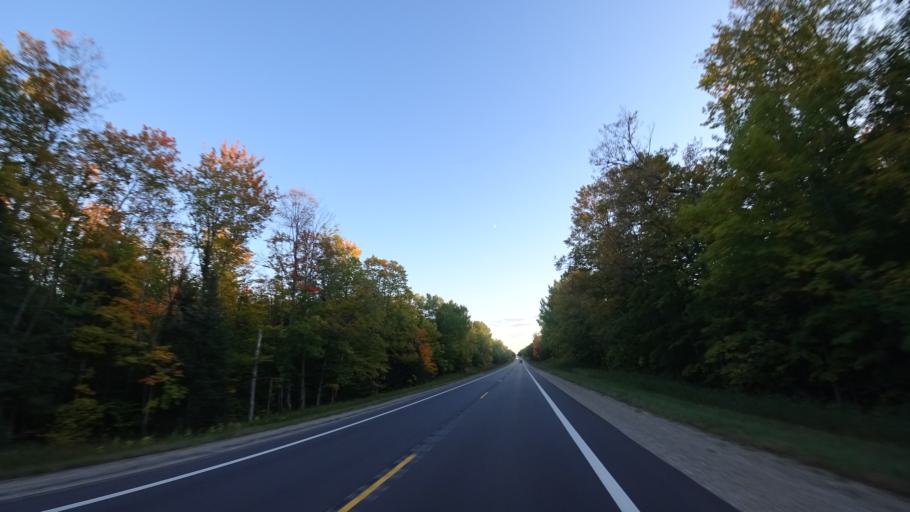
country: US
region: Michigan
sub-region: Luce County
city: Newberry
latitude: 46.2895
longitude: -85.0096
